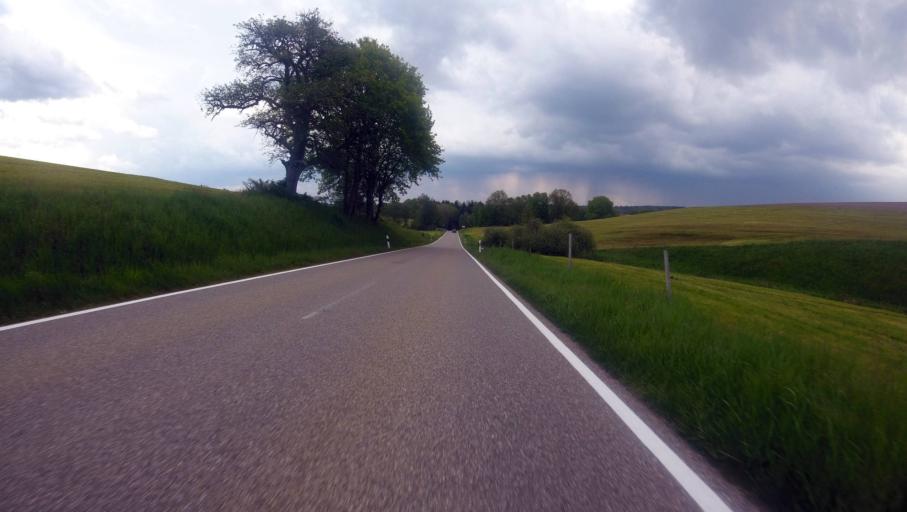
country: DE
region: Baden-Wuerttemberg
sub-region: Regierungsbezirk Stuttgart
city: Kaisersbach
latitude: 48.9464
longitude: 9.6227
